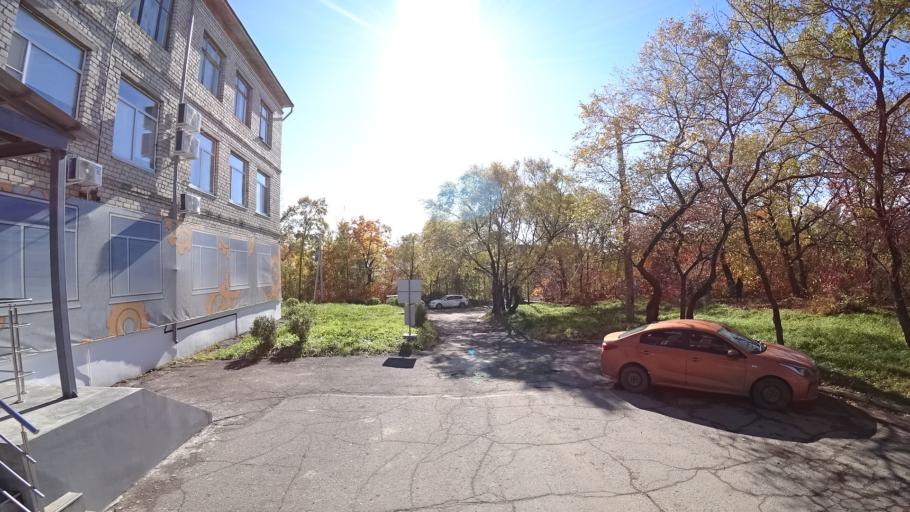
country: RU
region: Khabarovsk Krai
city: Amursk
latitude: 50.2197
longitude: 136.9062
